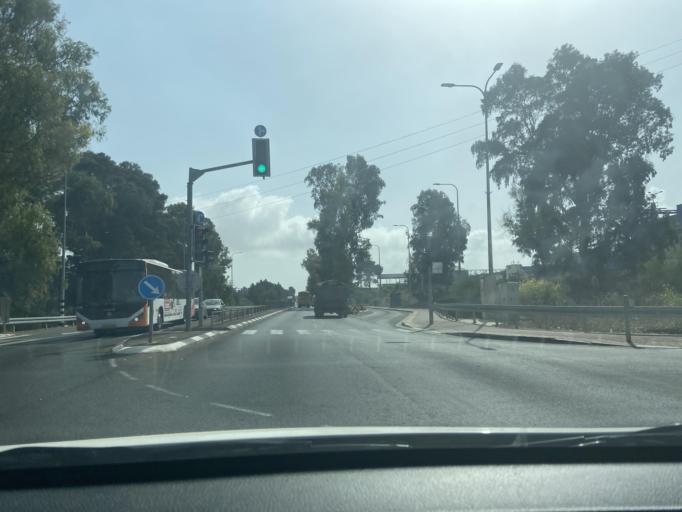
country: IL
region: Northern District
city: Nahariya
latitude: 33.0413
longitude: 35.1065
